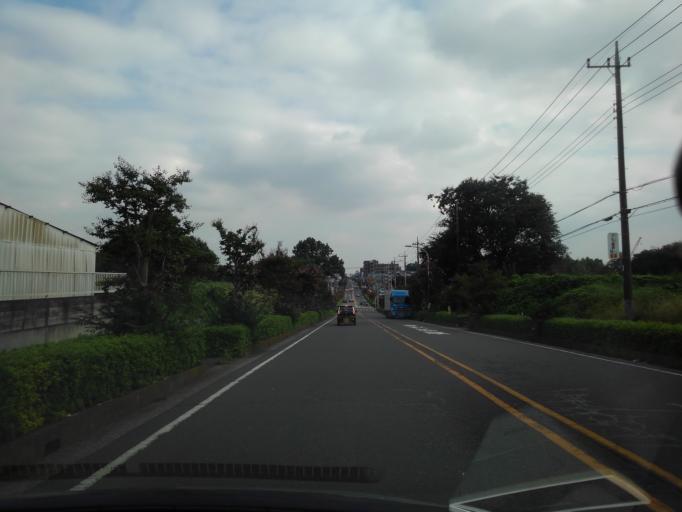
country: JP
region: Saitama
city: Tokorozawa
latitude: 35.8026
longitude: 139.5083
